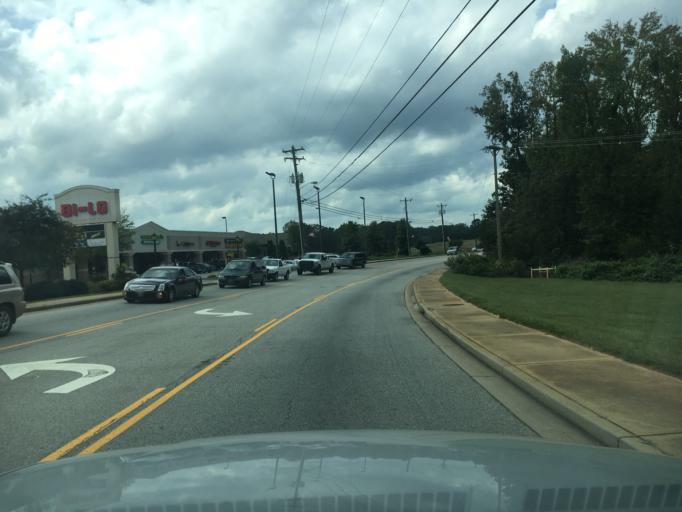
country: US
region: South Carolina
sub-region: Spartanburg County
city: Landrum
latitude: 35.1809
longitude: -82.1615
